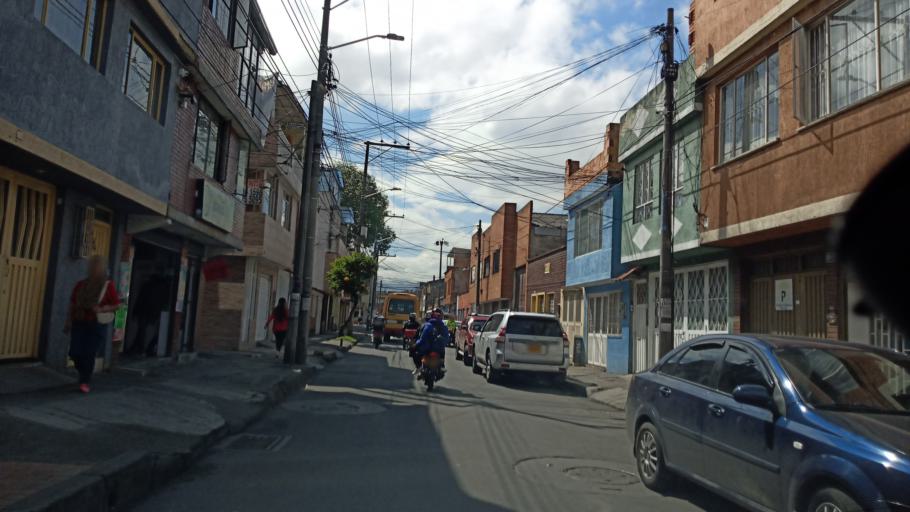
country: CO
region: Cundinamarca
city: Funza
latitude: 4.6789
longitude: -74.1358
